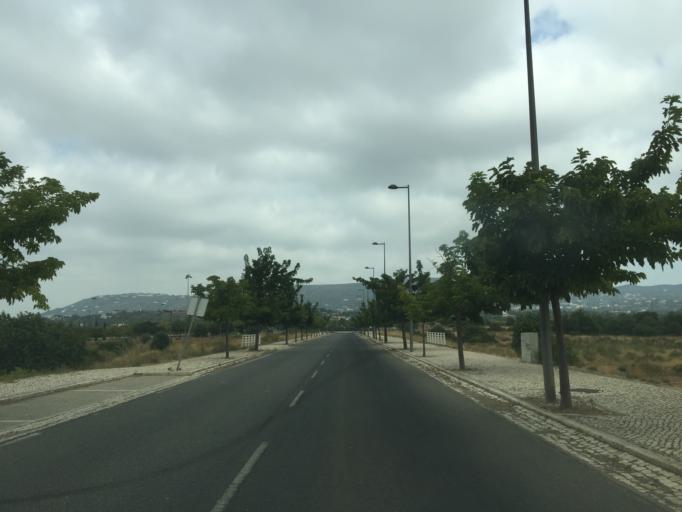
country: PT
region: Faro
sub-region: Faro
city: Santa Barbara de Nexe
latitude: 37.0839
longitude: -7.9783
